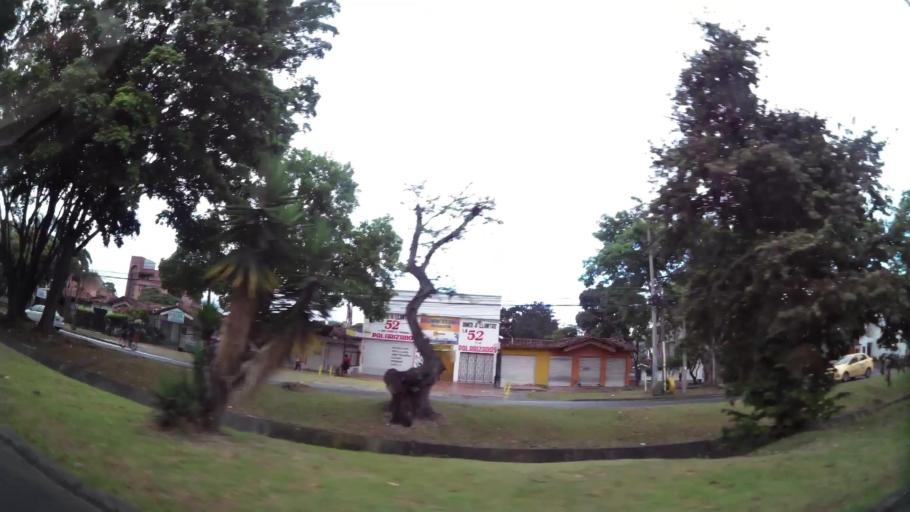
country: CO
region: Valle del Cauca
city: Cali
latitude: 3.4857
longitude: -76.5166
